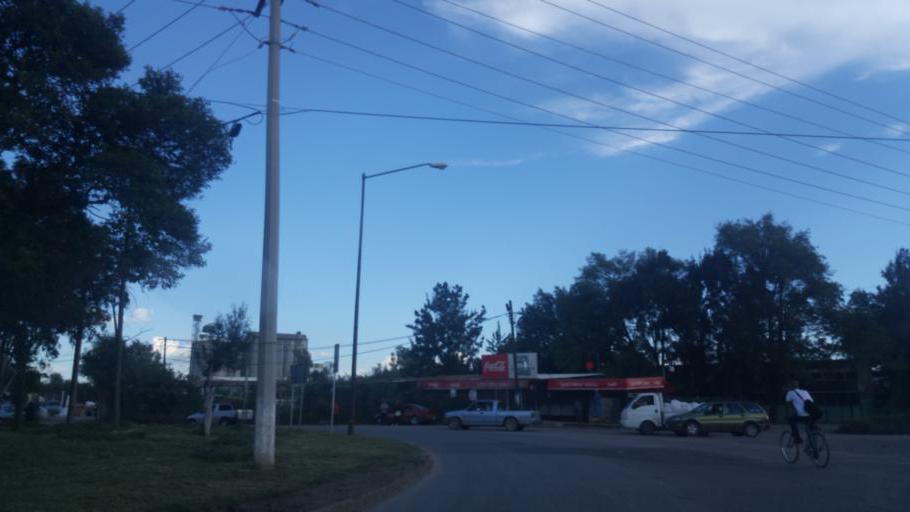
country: MX
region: Guanajuato
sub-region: Leon
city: San Jose de Duran (Los Troncoso)
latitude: 21.0952
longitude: -101.6955
